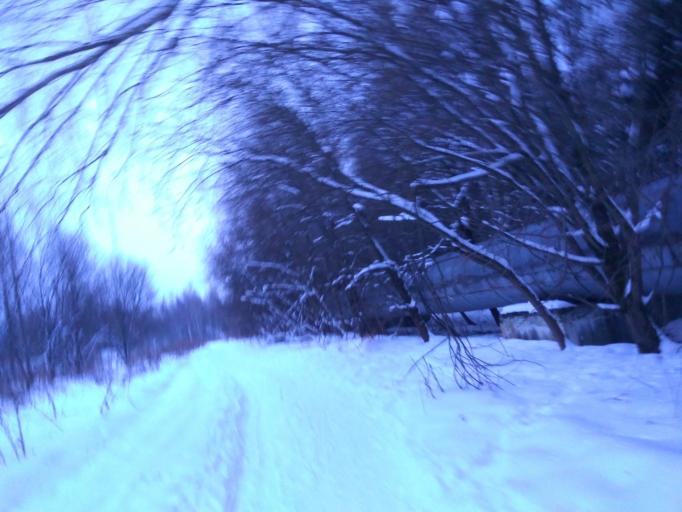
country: RU
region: Moscow
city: Biryulevo
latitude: 55.5918
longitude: 37.7007
